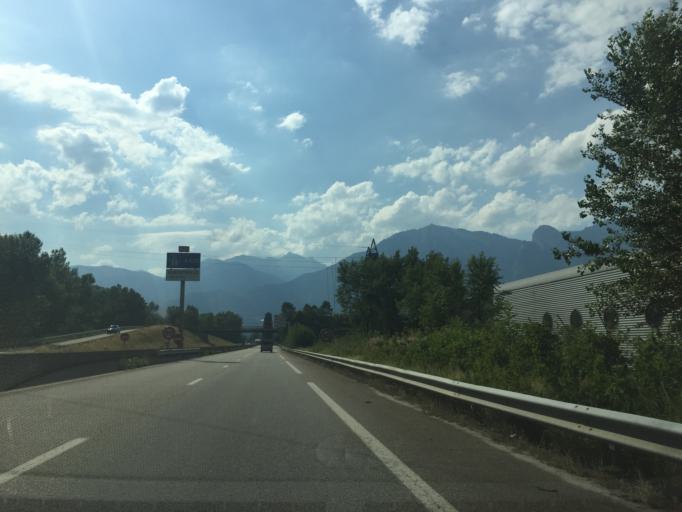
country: FR
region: Rhone-Alpes
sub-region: Departement de la Savoie
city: Albertville
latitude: 45.6614
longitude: 6.4137
